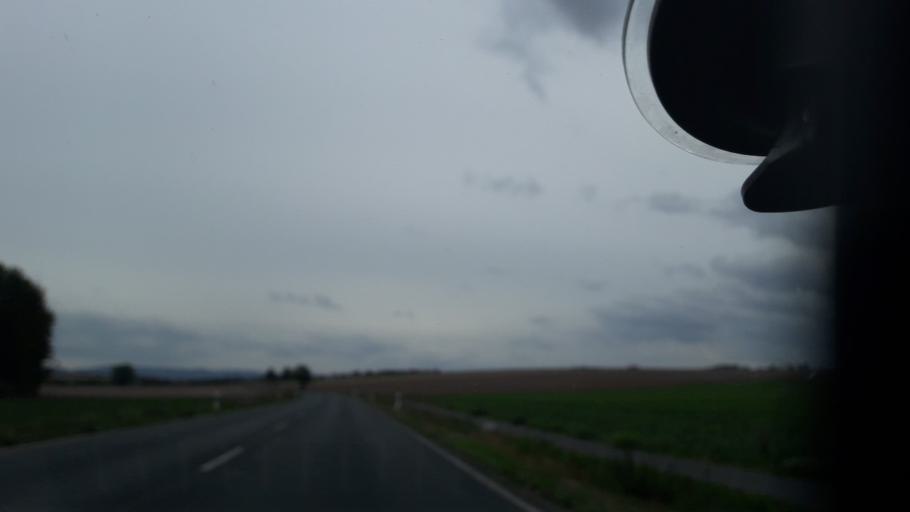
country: DE
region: Lower Saxony
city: Heiningen
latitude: 52.0619
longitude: 10.5502
